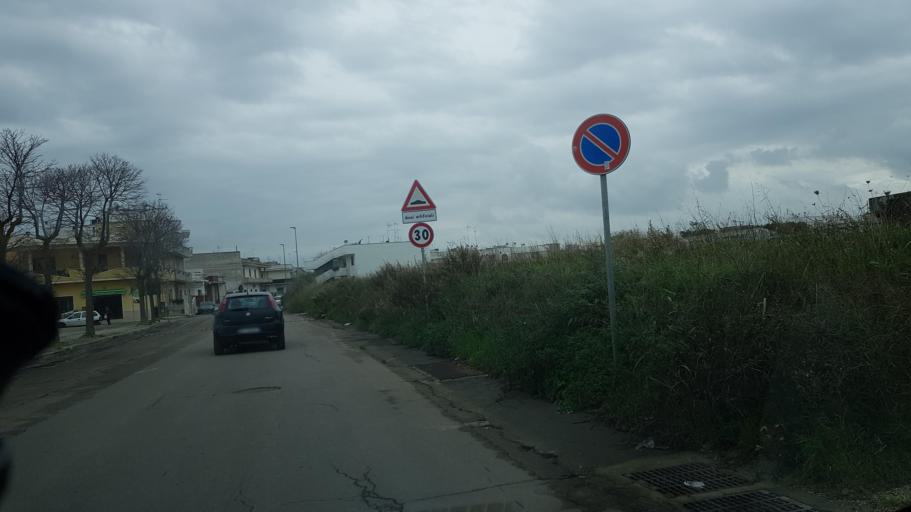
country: IT
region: Apulia
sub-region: Provincia di Lecce
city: Novoli
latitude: 40.3780
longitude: 18.0434
